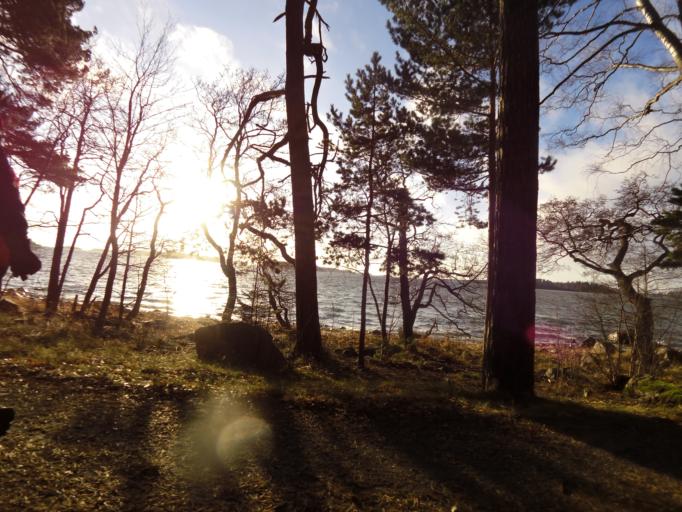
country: FI
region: Uusimaa
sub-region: Helsinki
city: Otaniemi
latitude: 60.1672
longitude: 24.8271
